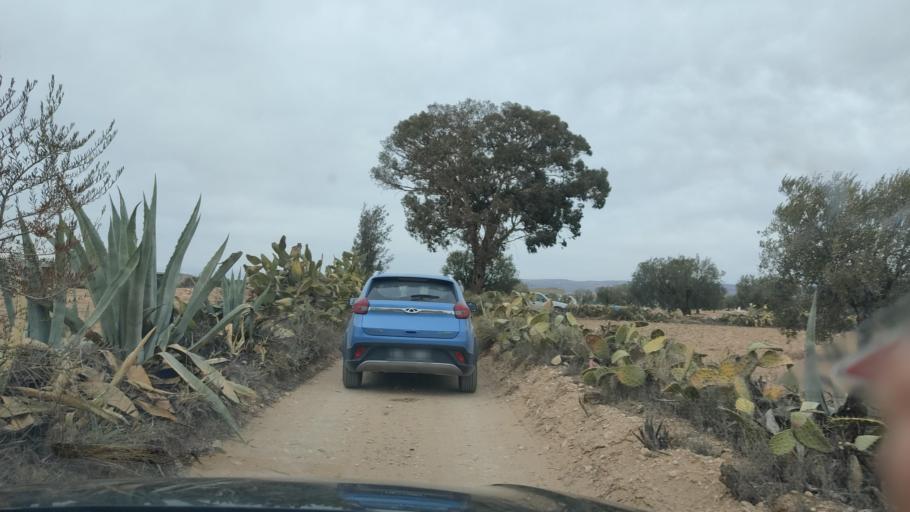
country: TN
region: Al Qasrayn
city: Kasserine
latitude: 35.2283
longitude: 8.9297
